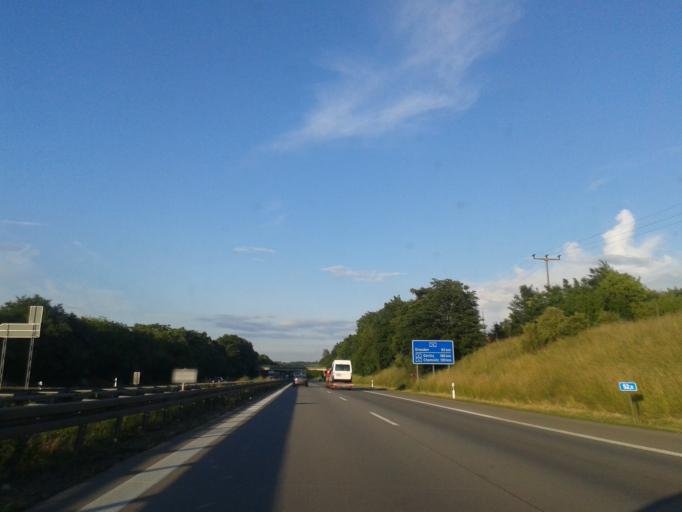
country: DE
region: Saxony
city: Grimma
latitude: 51.2574
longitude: 12.7370
